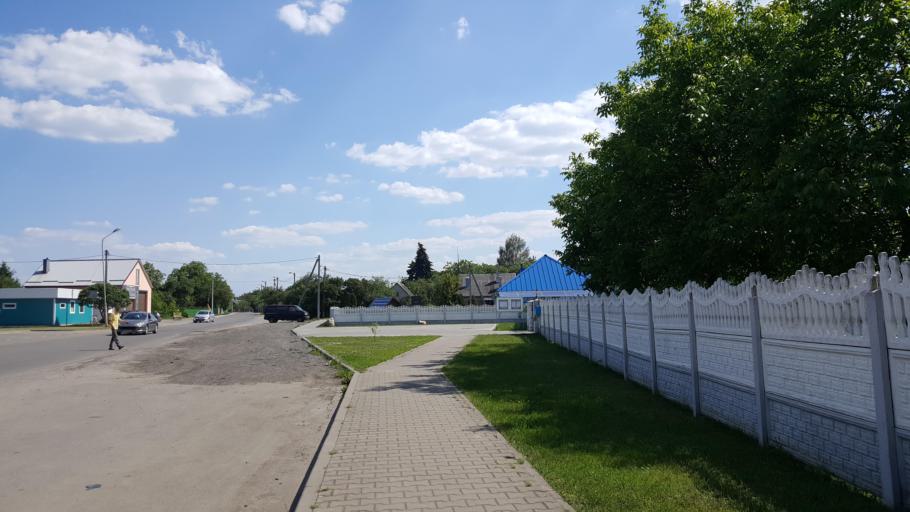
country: BY
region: Brest
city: Horad Kobryn
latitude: 52.2132
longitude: 24.3758
